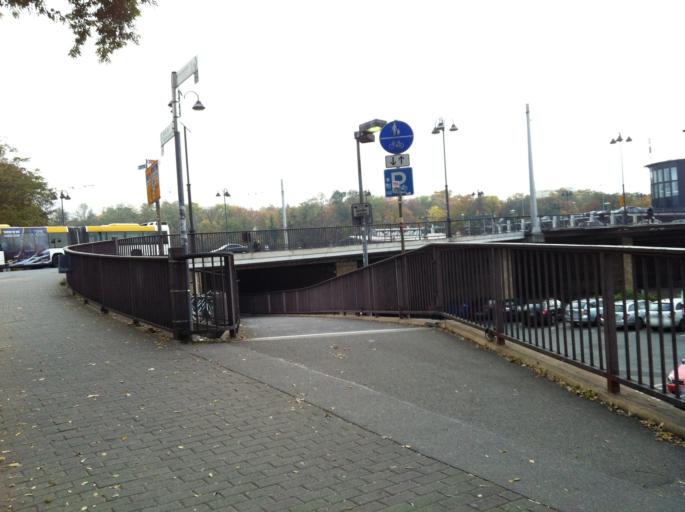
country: DE
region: Rheinland-Pfalz
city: Mainz
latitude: 50.0007
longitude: 8.2604
